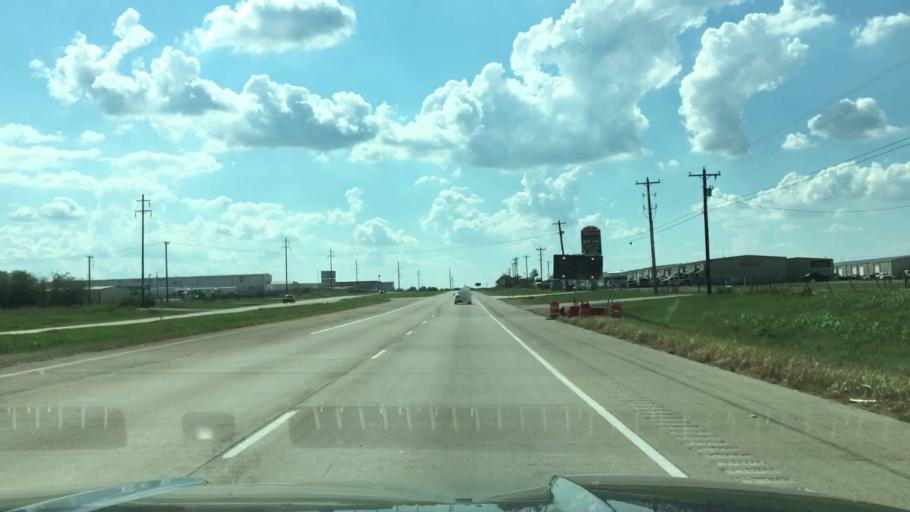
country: US
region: Texas
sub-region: Wise County
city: Rhome
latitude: 33.0370
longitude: -97.4330
